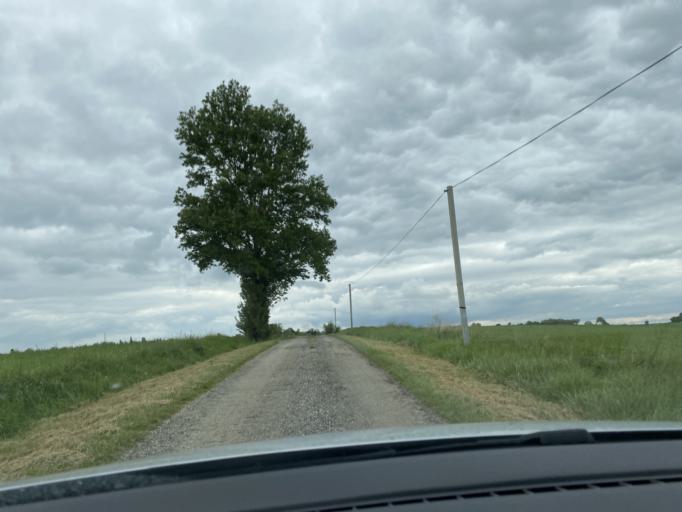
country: FR
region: Midi-Pyrenees
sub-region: Departement de la Haute-Garonne
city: Nailloux
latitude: 43.3641
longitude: 1.6398
